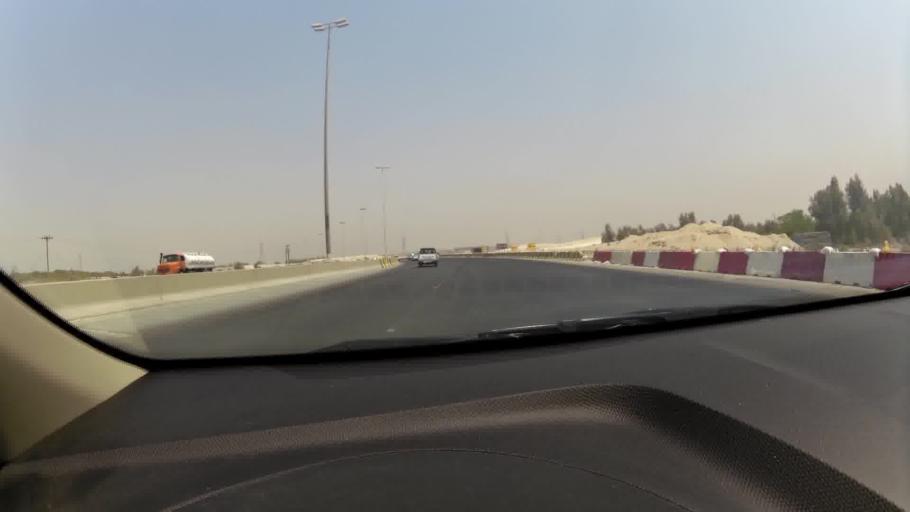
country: KW
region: Muhafazat al Jahra'
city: Al Jahra'
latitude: 29.2859
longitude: 47.7775
